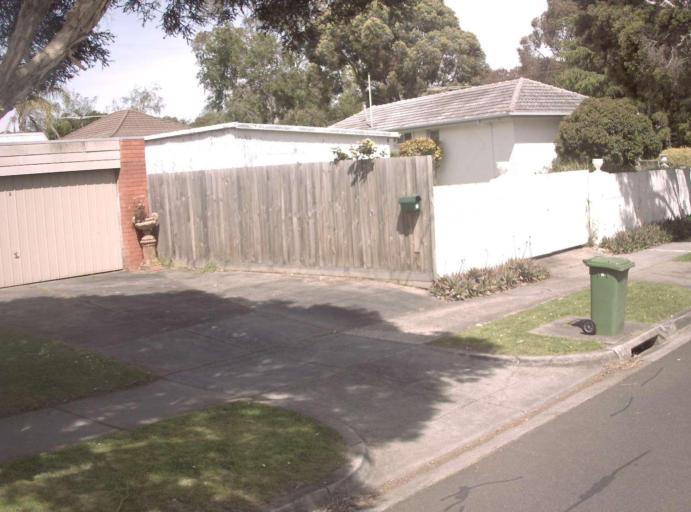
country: AU
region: Victoria
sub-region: Maroondah
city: Croydon Hills
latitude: -37.7855
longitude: 145.2691
